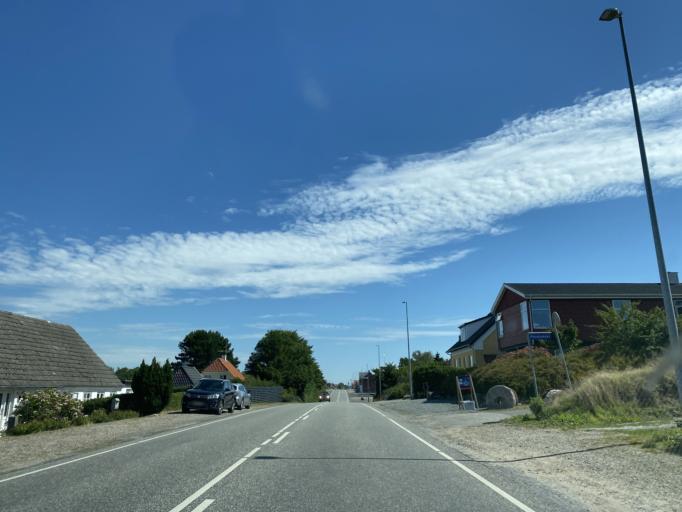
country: DK
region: South Denmark
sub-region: Faaborg-Midtfyn Kommune
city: Faaborg
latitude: 55.1094
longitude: 10.1635
